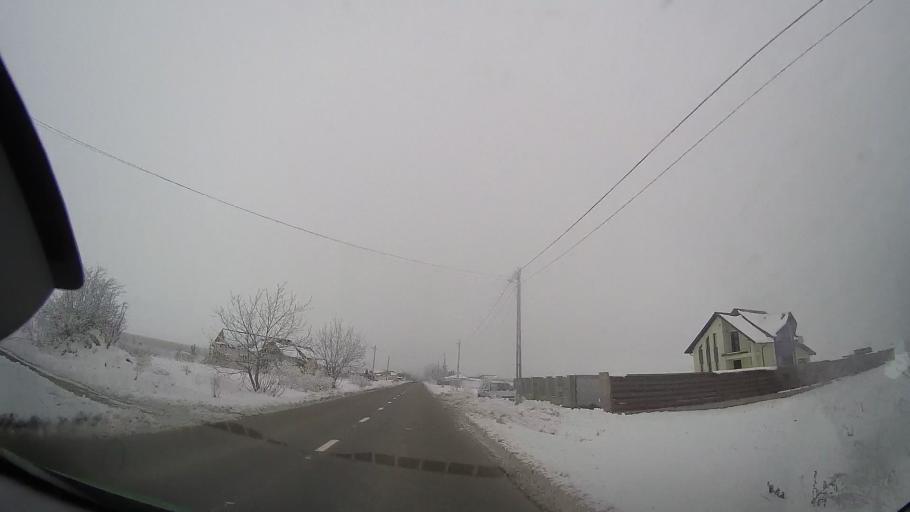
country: RO
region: Neamt
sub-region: Comuna Horia
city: Cotu Vames
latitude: 46.8941
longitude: 26.9617
